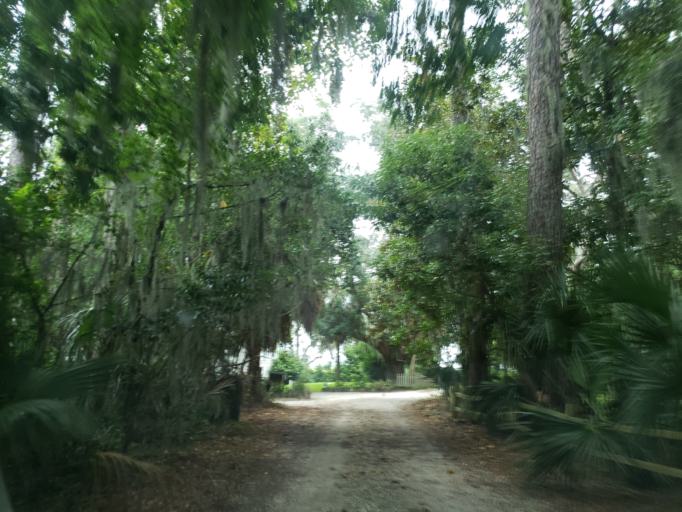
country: US
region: Georgia
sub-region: Chatham County
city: Wilmington Island
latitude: 32.0186
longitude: -80.9498
